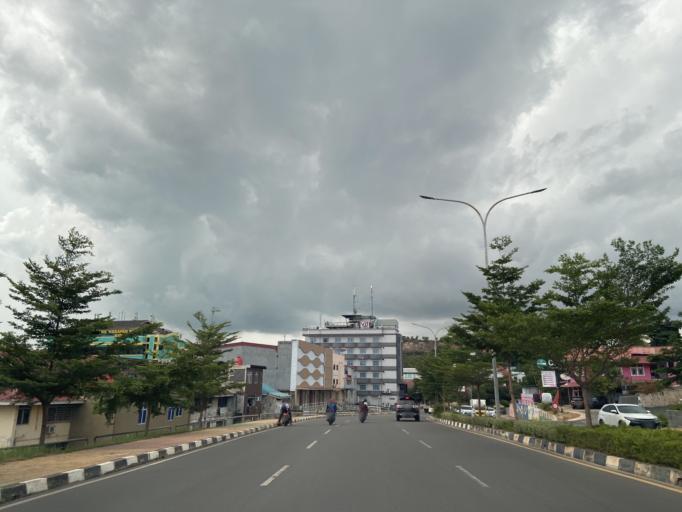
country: SG
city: Singapore
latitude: 1.1475
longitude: 104.0151
